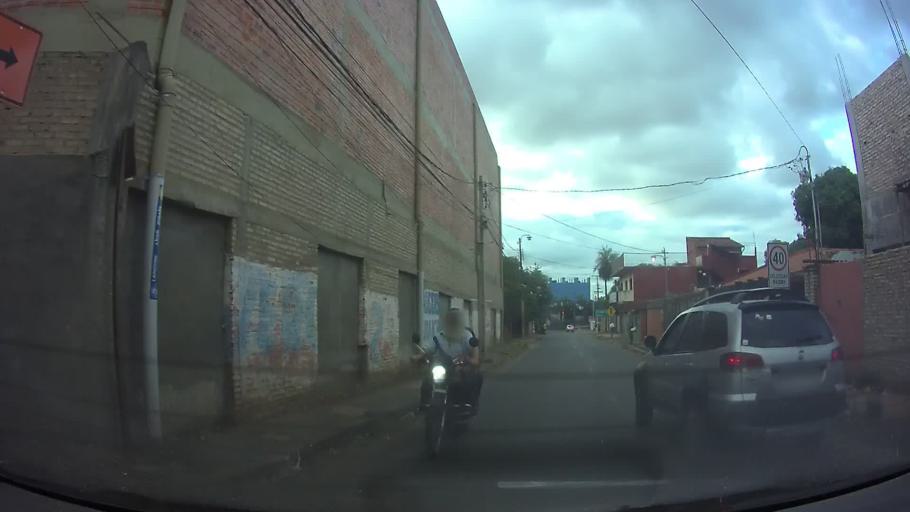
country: PY
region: Central
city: Fernando de la Mora
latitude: -25.3144
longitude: -57.5545
